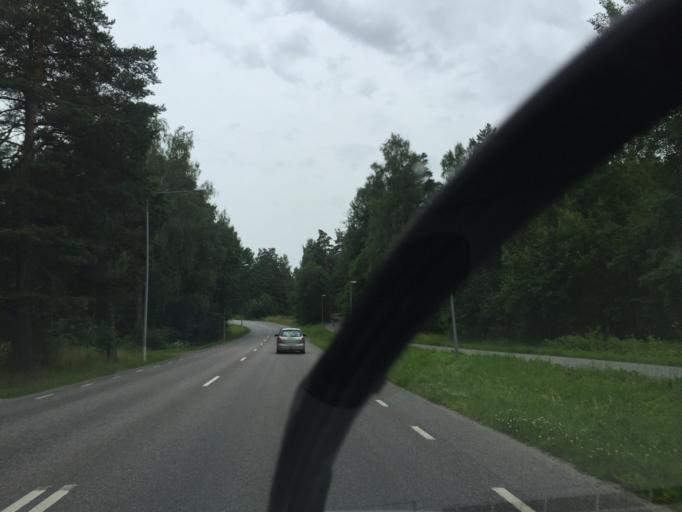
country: SE
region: OErebro
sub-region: Orebro Kommun
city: Orebro
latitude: 59.2473
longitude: 15.1987
